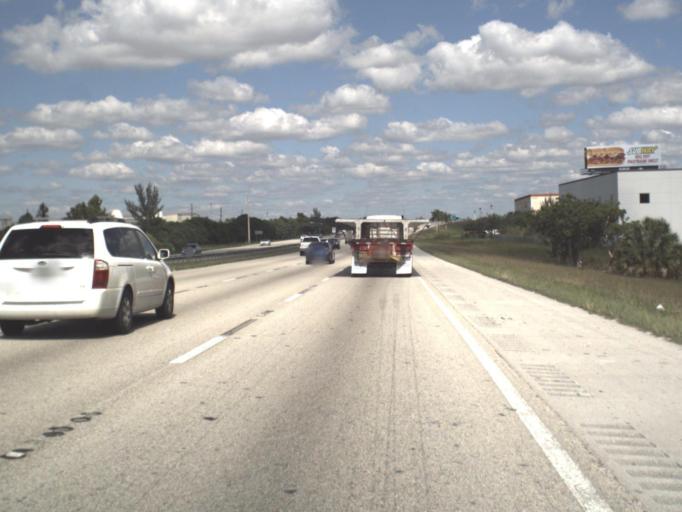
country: US
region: Florida
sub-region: Miami-Dade County
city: Hialeah Gardens
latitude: 25.8853
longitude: -80.3885
